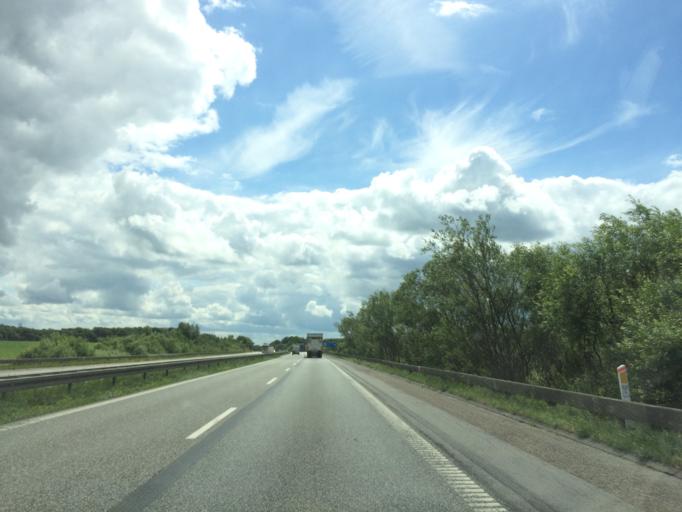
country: DK
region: North Denmark
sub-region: Mariagerfjord Kommune
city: Hobro
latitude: 56.6309
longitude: 9.7340
